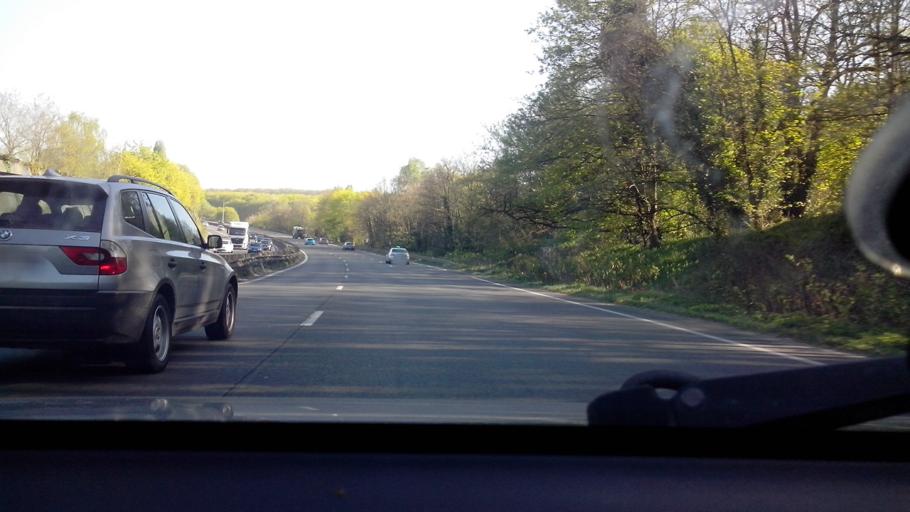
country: FR
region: Ile-de-France
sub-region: Departement de l'Essonne
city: Bievres
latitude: 48.7623
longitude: 2.2280
